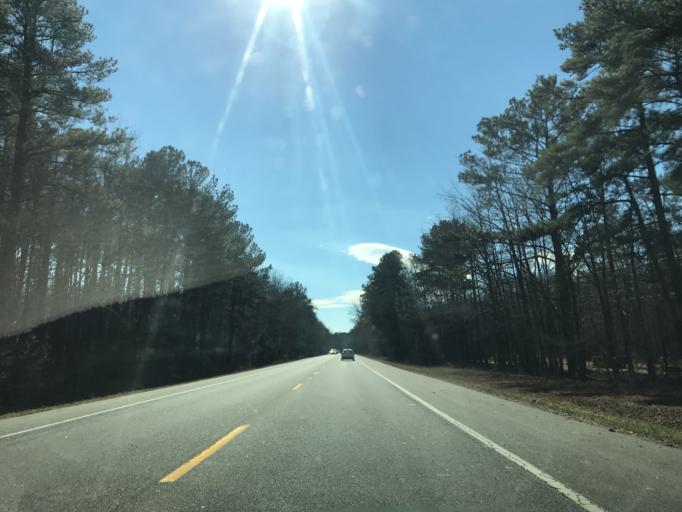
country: US
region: Maryland
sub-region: Queen Anne's County
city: Stevensville
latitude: 38.9457
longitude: -76.3523
